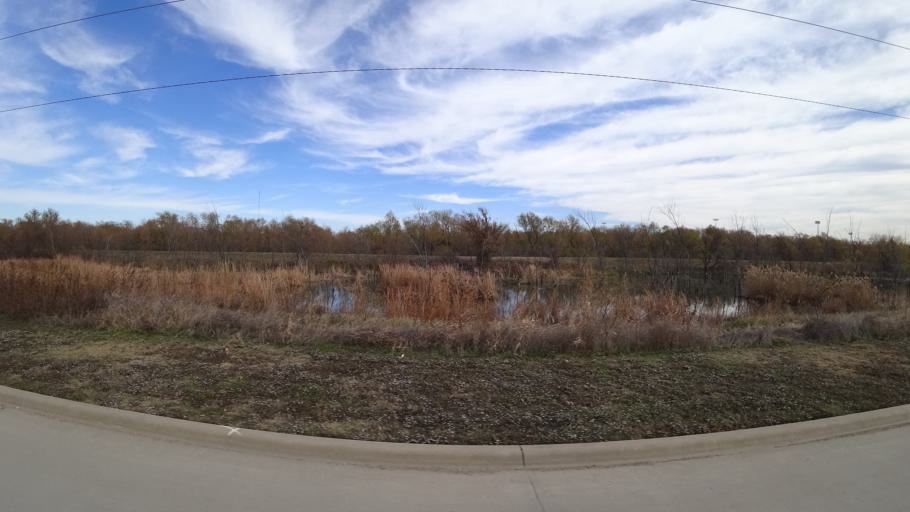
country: US
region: Texas
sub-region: Denton County
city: Lewisville
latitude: 33.0307
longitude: -96.9759
